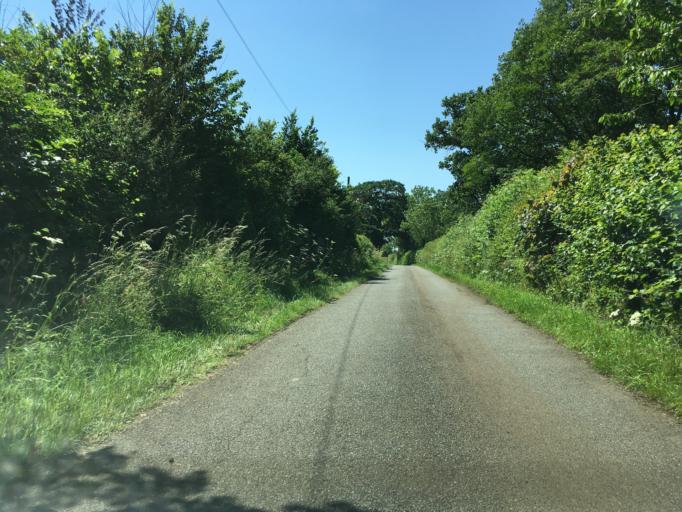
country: GB
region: England
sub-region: Northamptonshire
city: Brackley
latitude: 52.0180
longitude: -1.0703
